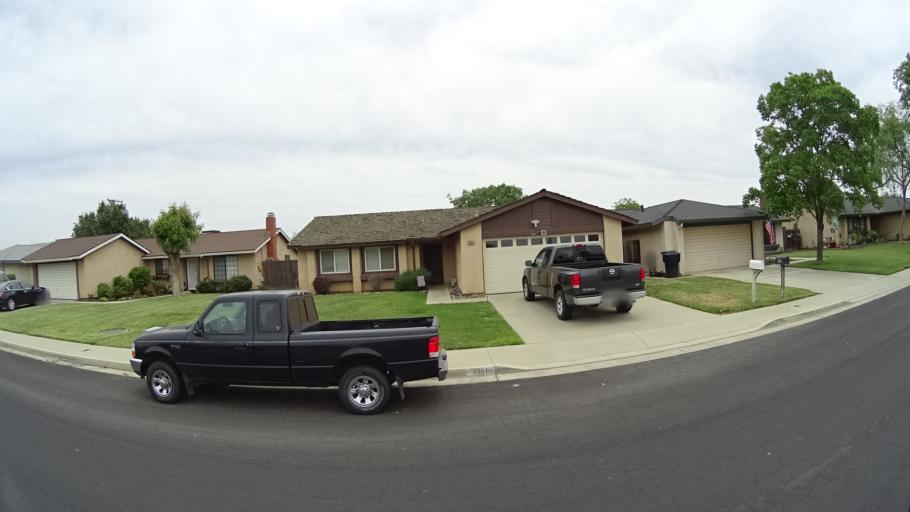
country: US
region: California
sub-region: Kings County
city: Hanford
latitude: 36.3487
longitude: -119.6285
